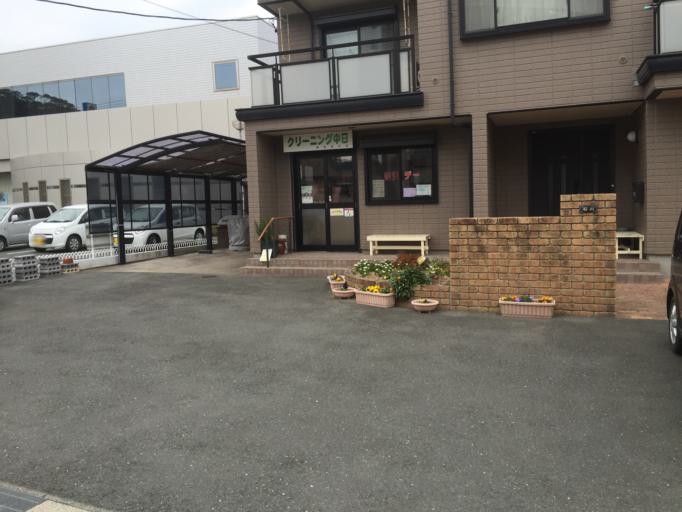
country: JP
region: Shizuoka
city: Kosai-shi
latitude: 34.7175
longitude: 137.5435
